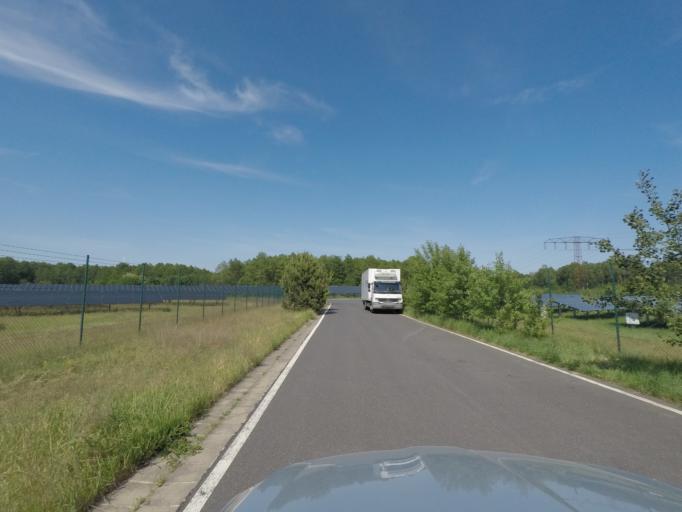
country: DE
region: Brandenburg
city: Britz
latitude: 52.8578
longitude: 13.7706
